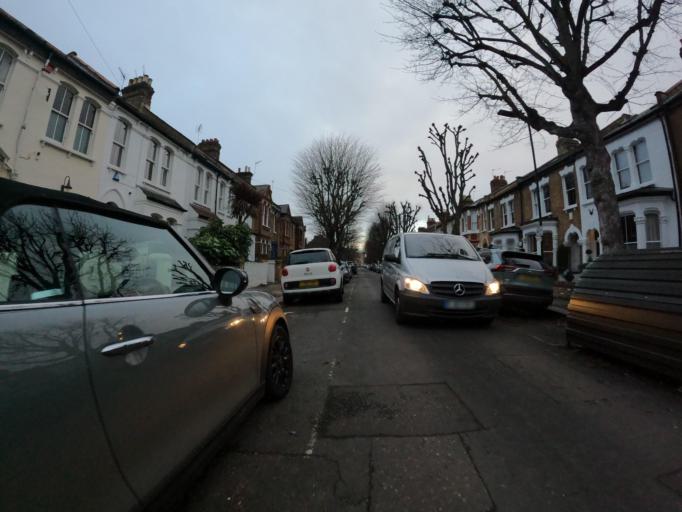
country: GB
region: England
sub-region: Greater London
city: Acton
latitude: 51.4993
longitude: -0.2661
